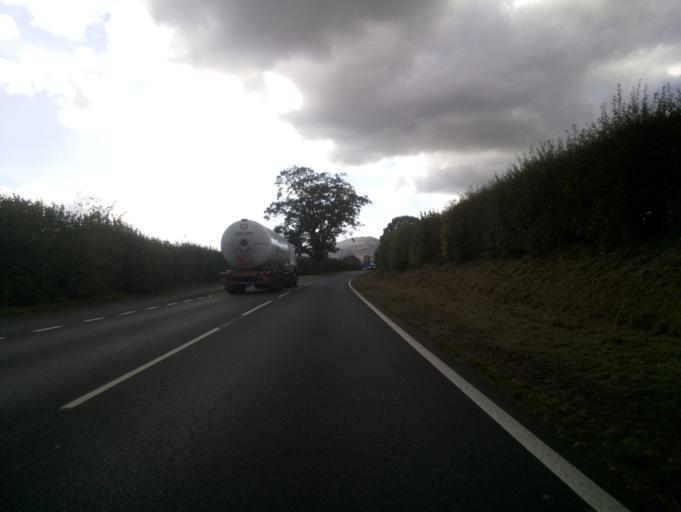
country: GB
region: Wales
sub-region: Sir Powys
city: Brecon
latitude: 51.9261
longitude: -3.4583
